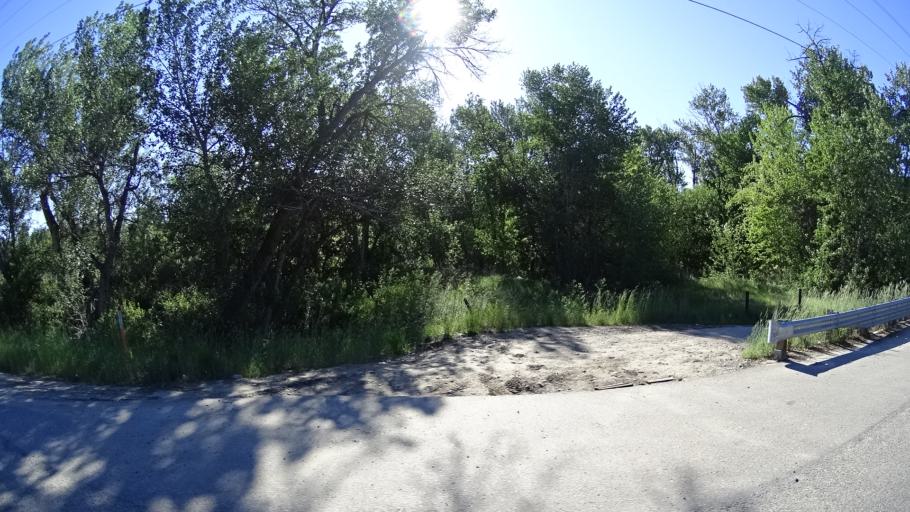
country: US
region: Idaho
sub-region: Ada County
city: Eagle
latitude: 43.6886
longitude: -116.4137
